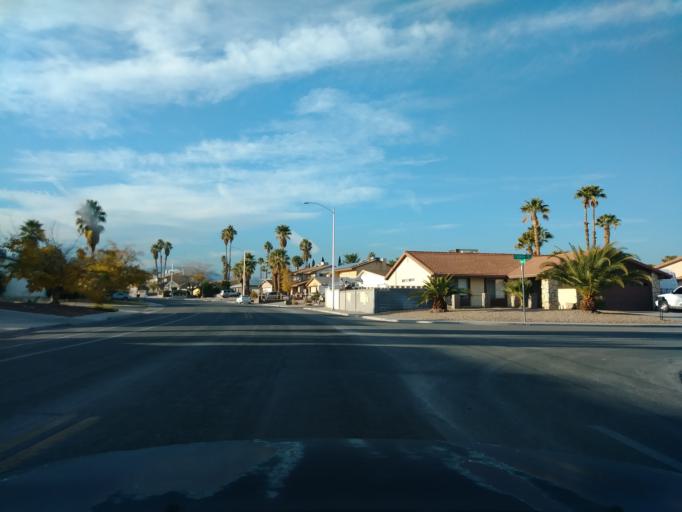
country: US
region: Nevada
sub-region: Clark County
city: Spring Valley
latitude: 36.1694
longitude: -115.2377
